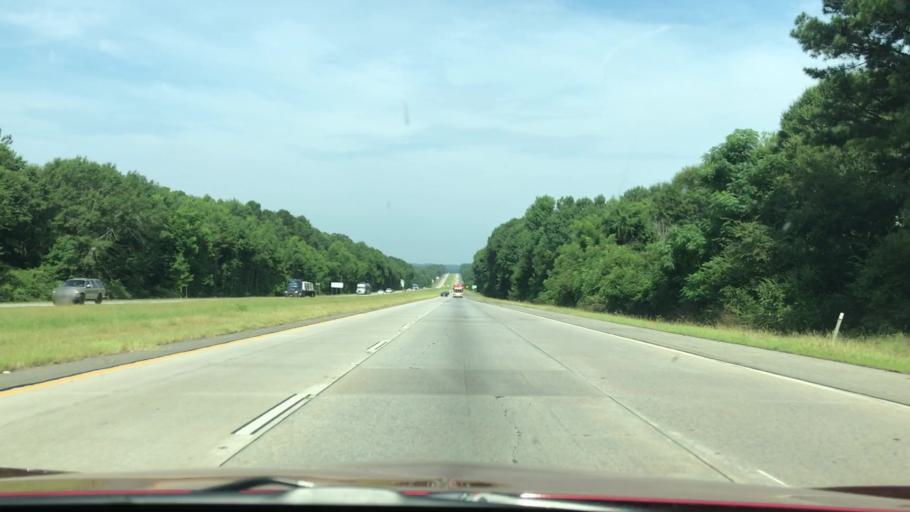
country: US
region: Georgia
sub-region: Greene County
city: Union Point
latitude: 33.5449
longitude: -83.0869
